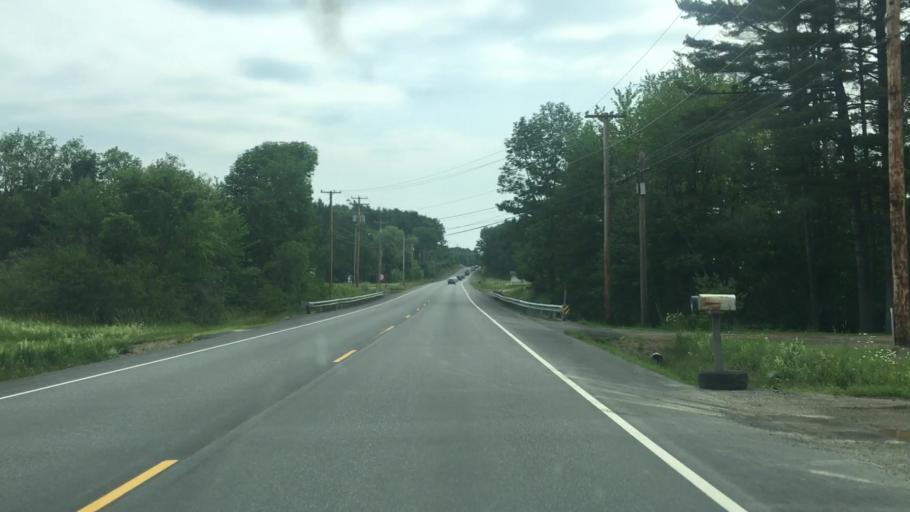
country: US
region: Maine
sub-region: Waldo County
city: Belfast
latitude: 44.4131
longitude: -69.0610
